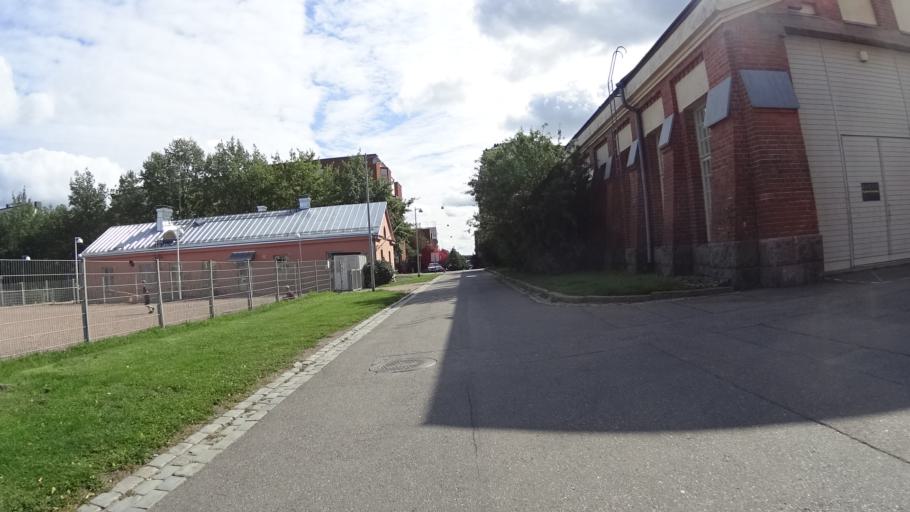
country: FI
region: Uusimaa
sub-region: Helsinki
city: Helsinki
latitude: 60.1672
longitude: 24.9710
